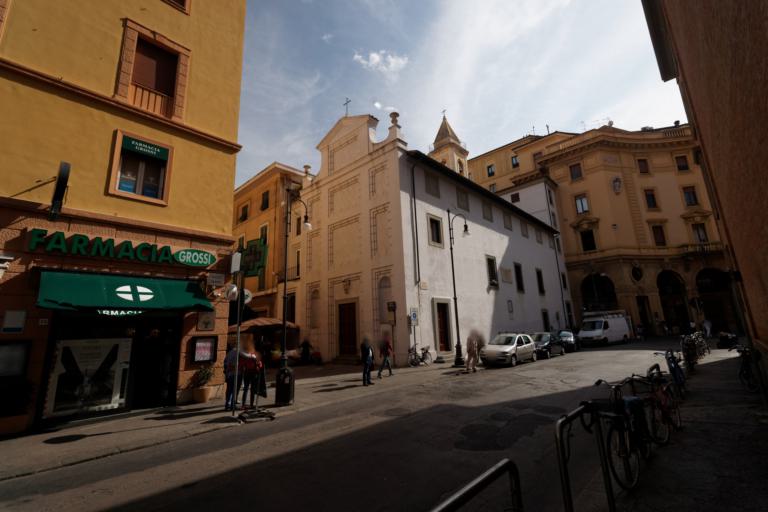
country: IT
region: Tuscany
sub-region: Provincia di Livorno
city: Livorno
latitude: 43.5502
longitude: 10.3098
